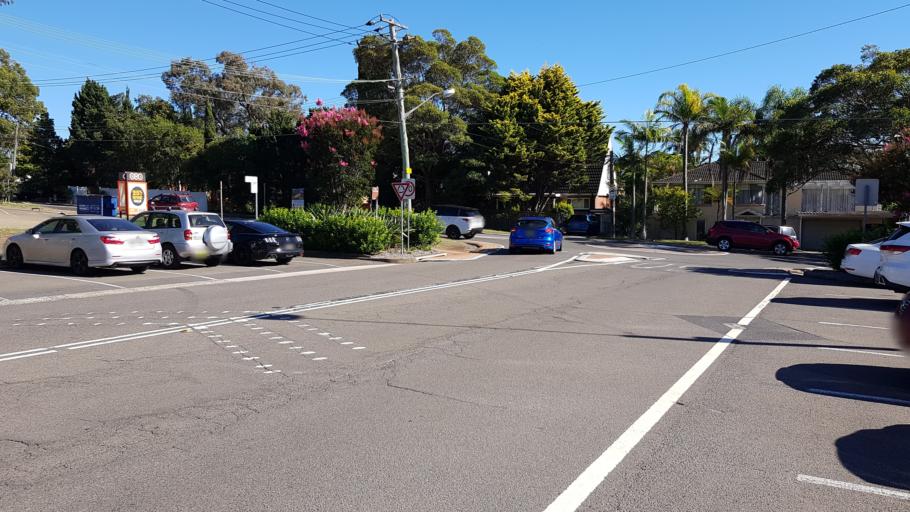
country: AU
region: New South Wales
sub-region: Pittwater
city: Warriewood
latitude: -33.6954
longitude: 151.2801
